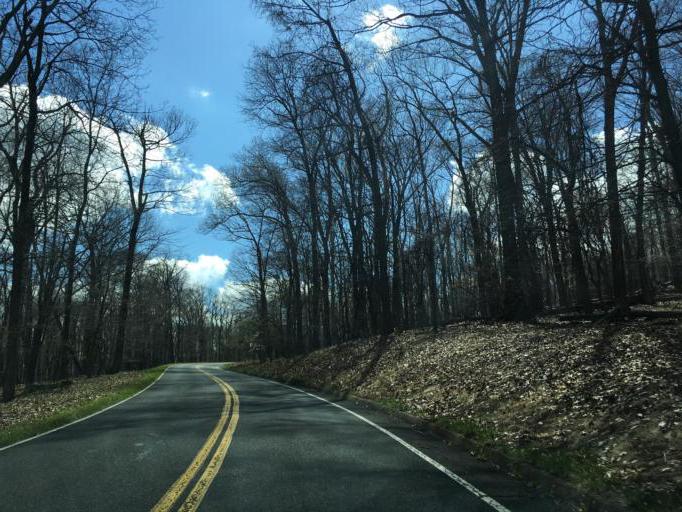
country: US
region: Maryland
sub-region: Frederick County
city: Thurmont
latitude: 39.6437
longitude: -77.4627
